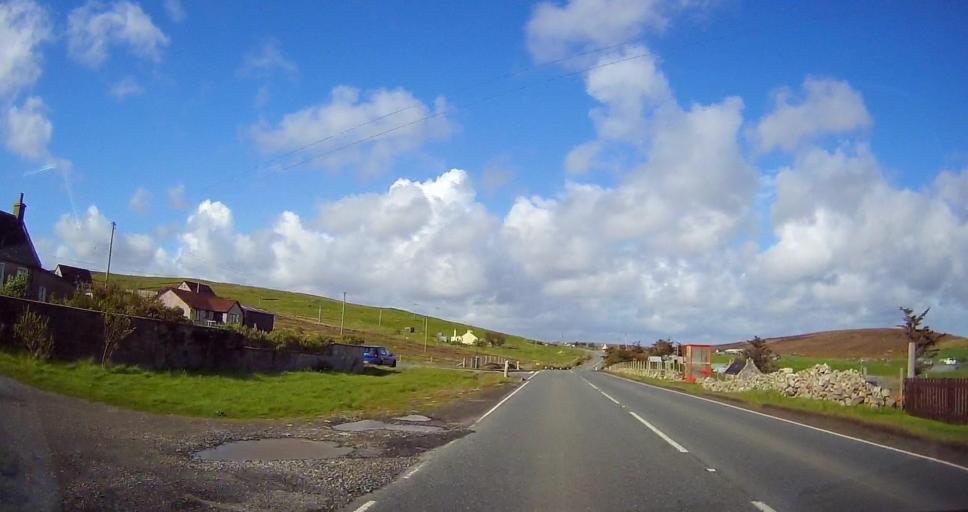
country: GB
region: Scotland
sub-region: Shetland Islands
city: Lerwick
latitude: 60.2346
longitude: -1.2337
